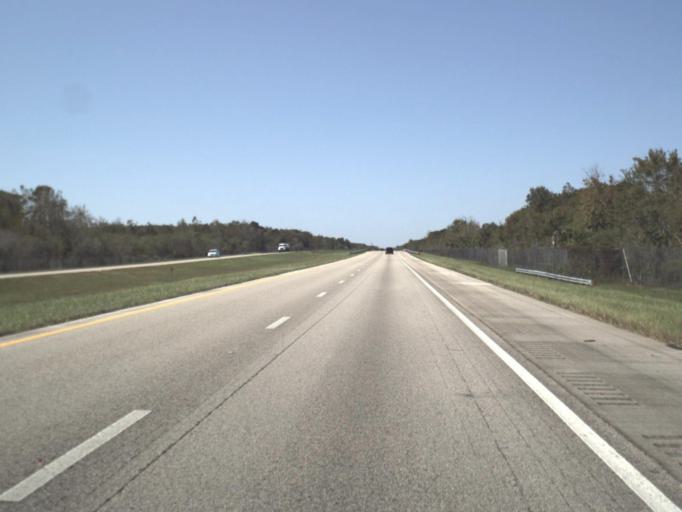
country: US
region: Florida
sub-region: Collier County
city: Orangetree
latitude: 26.1539
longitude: -81.4114
